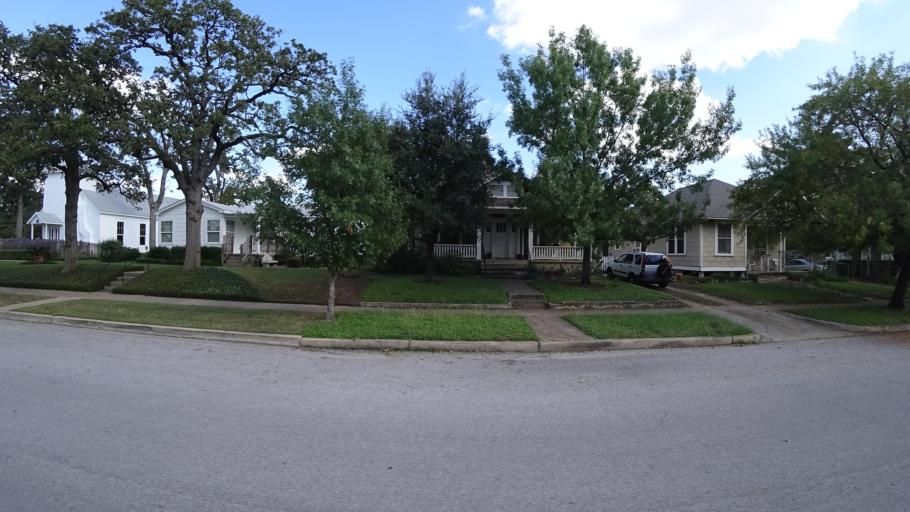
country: US
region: Texas
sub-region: Travis County
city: Austin
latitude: 30.3039
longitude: -97.7350
